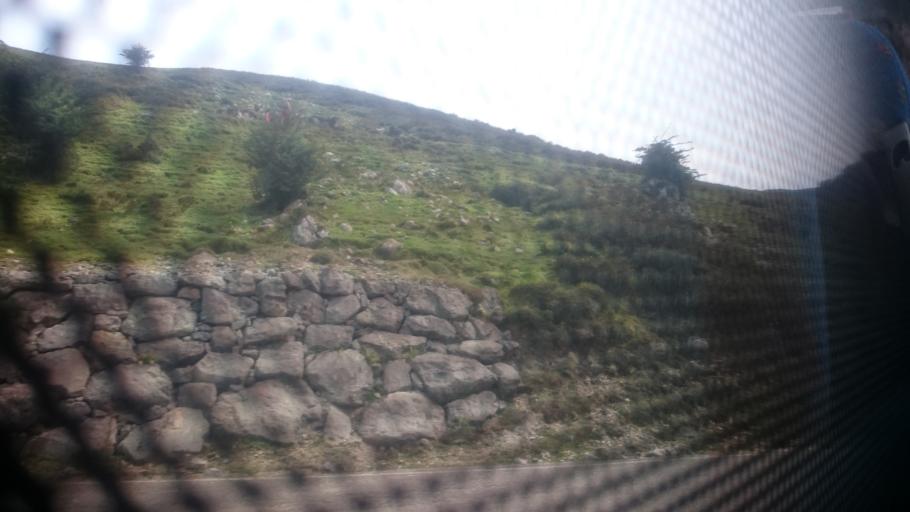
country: ES
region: Asturias
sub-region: Province of Asturias
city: Amieva
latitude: 43.2751
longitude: -4.9859
